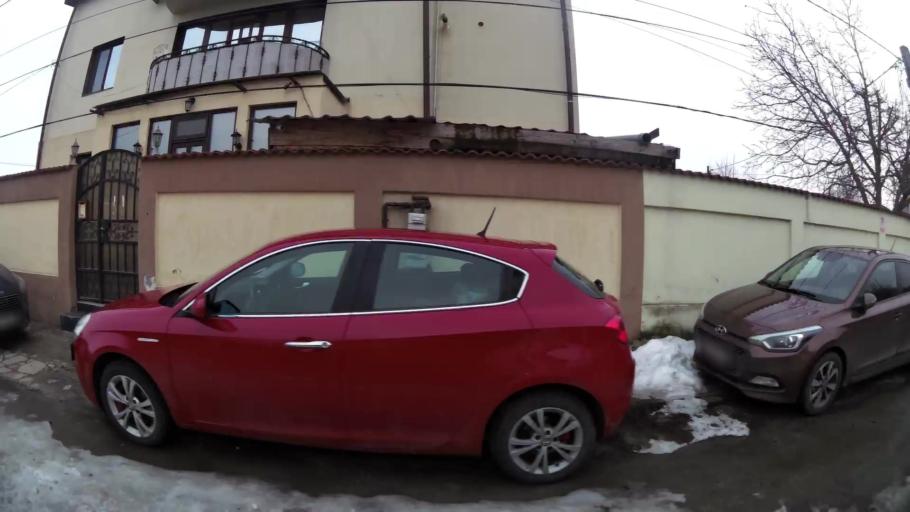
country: RO
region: Ilfov
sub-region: Comuna Tunari
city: Tunari
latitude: 44.5449
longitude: 26.1295
